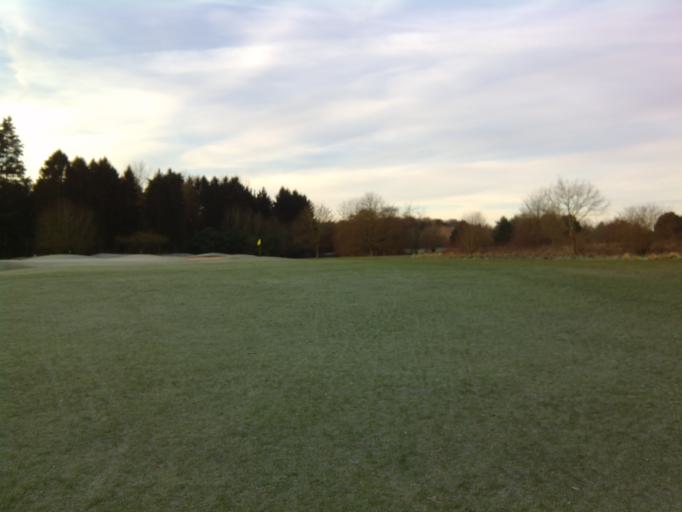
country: BE
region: Wallonia
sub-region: Province du Brabant Wallon
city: Louvain-la-Neuve
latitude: 50.6840
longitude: 4.6125
